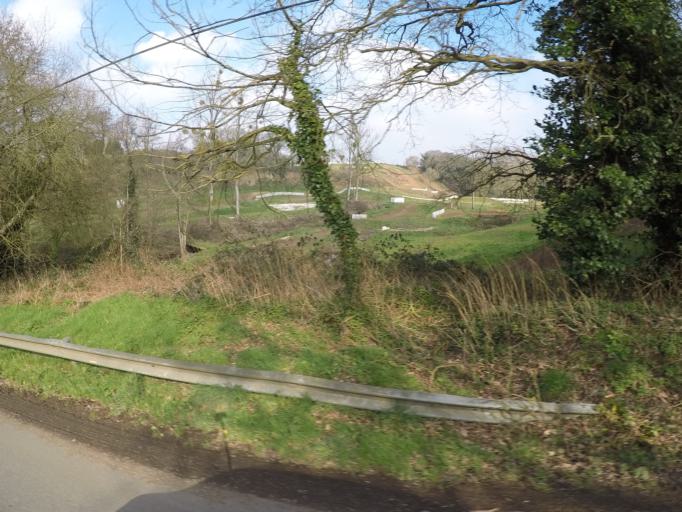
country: FR
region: Brittany
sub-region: Departement des Cotes-d'Armor
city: Goudelin
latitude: 48.6101
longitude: -3.0332
